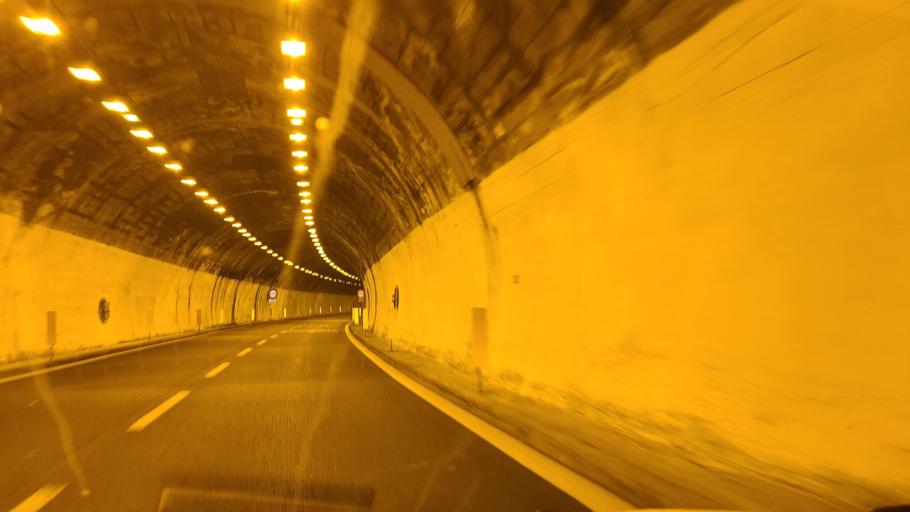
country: IT
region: Liguria
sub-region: Provincia di Imperia
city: Imperia
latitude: 43.8993
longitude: 8.0473
